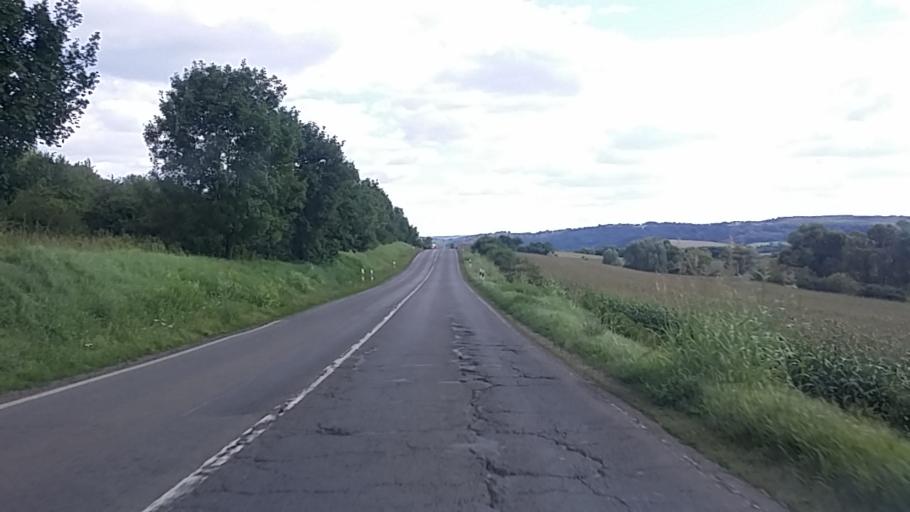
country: HU
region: Baranya
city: Sasd
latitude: 46.2313
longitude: 18.1215
